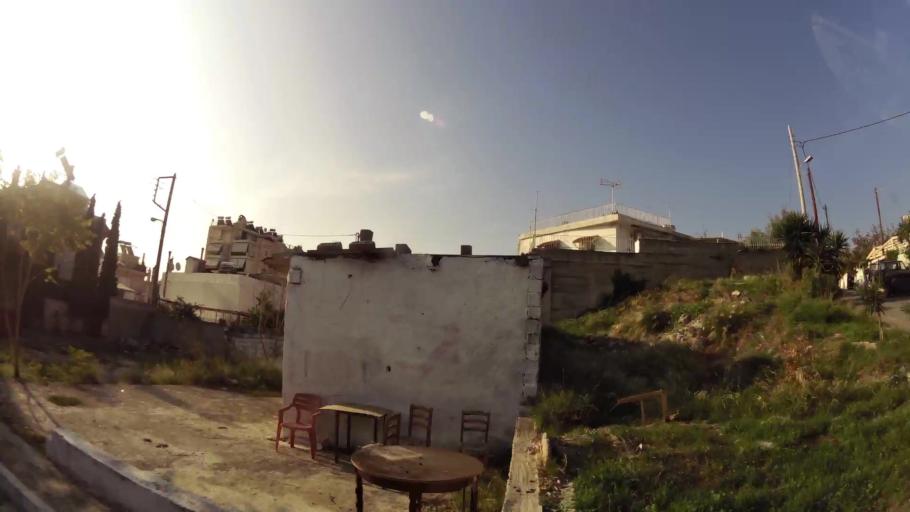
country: GR
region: Attica
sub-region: Nomos Piraios
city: Keratsini
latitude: 37.9677
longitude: 23.6332
